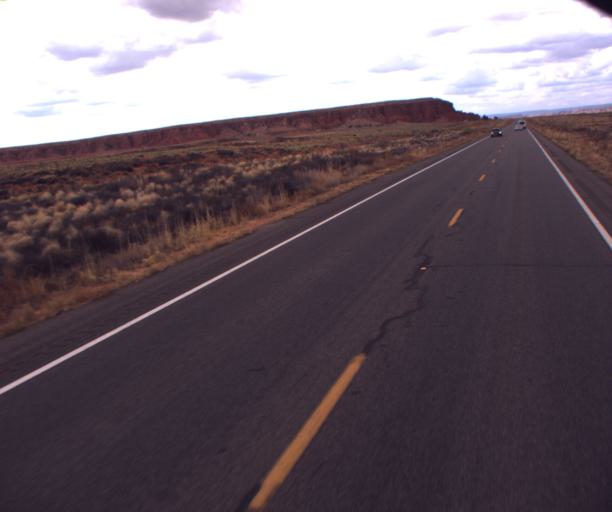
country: US
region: Arizona
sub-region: Navajo County
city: Kayenta
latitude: 36.7804
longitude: -109.9923
